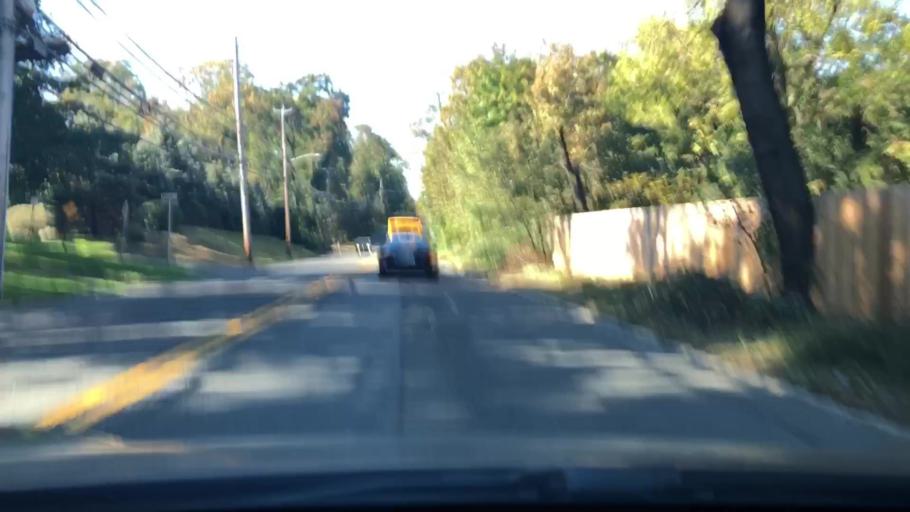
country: US
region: New York
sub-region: Westchester County
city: Harrison
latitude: 40.9929
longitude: -73.7143
